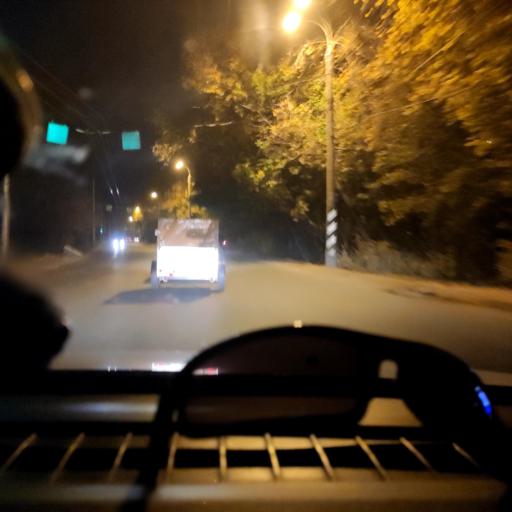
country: RU
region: Samara
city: Samara
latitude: 53.1567
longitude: 50.0913
